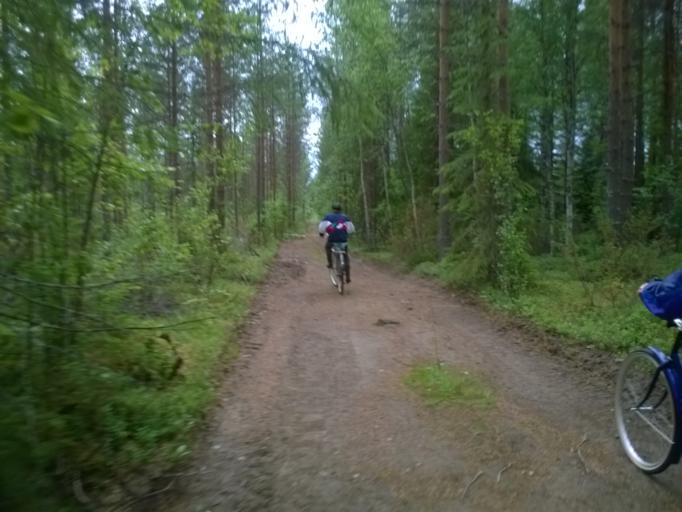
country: FI
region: Kainuu
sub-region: Kehys-Kainuu
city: Kuhmo
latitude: 64.1295
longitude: 29.4028
